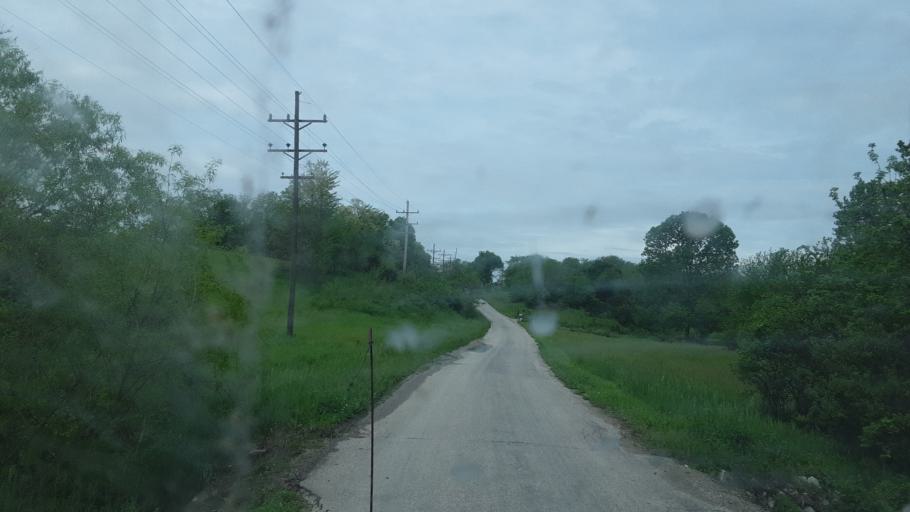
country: US
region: Missouri
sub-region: Clark County
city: Kahoka
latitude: 40.4241
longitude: -91.6023
